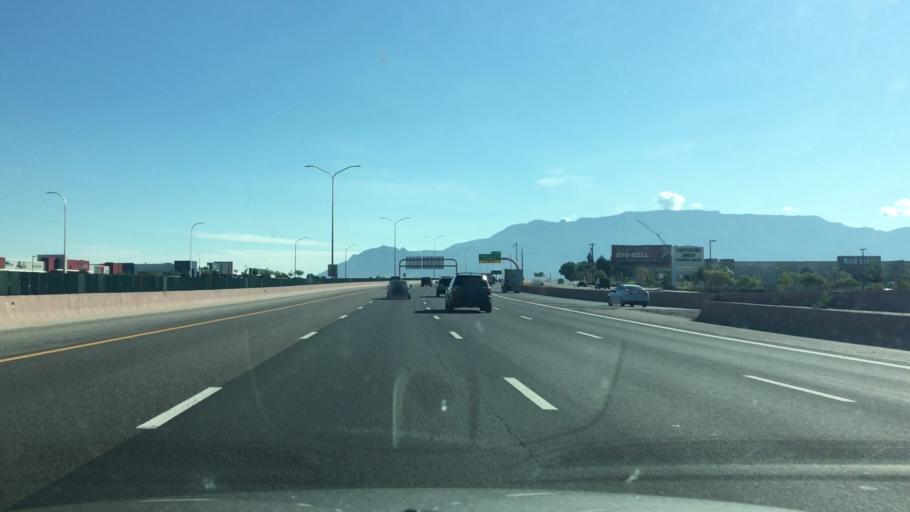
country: US
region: New Mexico
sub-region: Bernalillo County
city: Lee Acres
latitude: 35.1263
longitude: -106.6201
